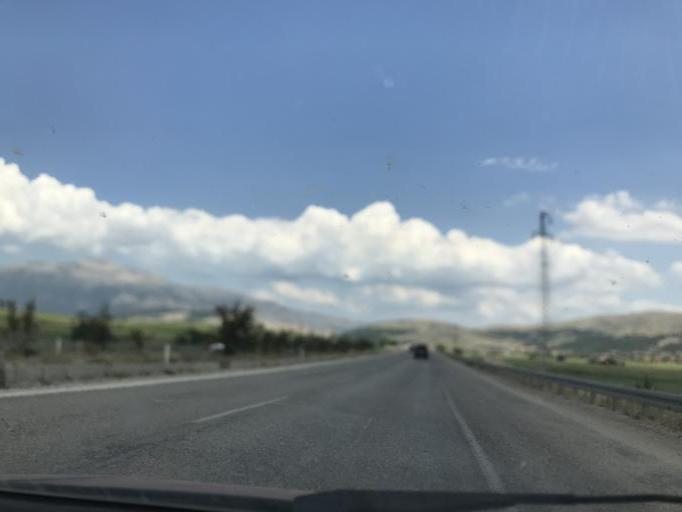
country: TR
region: Denizli
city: Serinhisar
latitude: 37.6160
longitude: 29.1747
